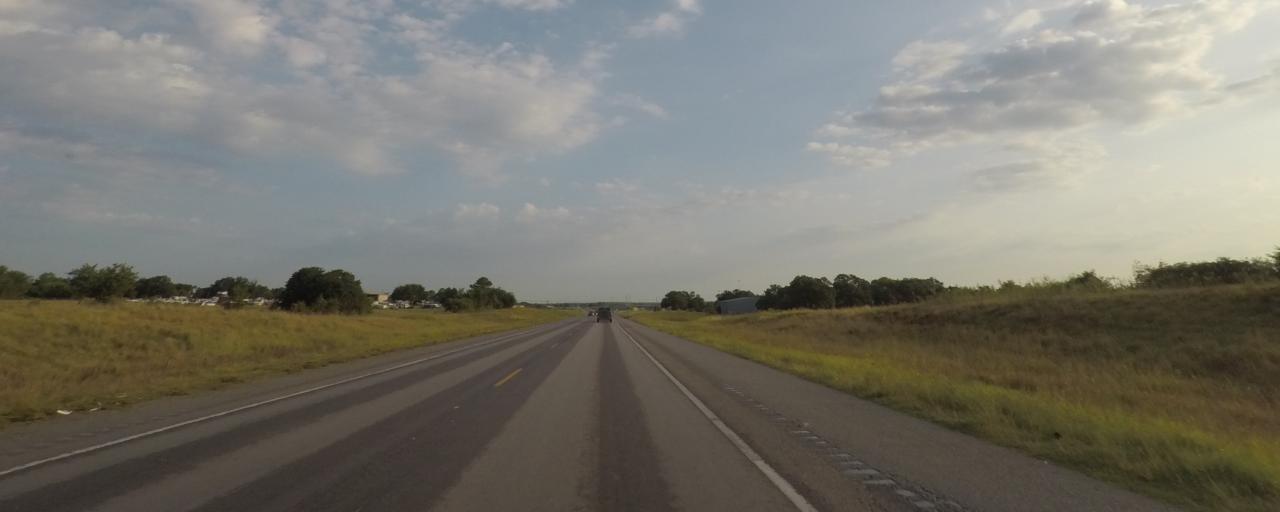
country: US
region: Oklahoma
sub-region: Stephens County
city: Meridian
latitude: 34.4563
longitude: -97.9741
